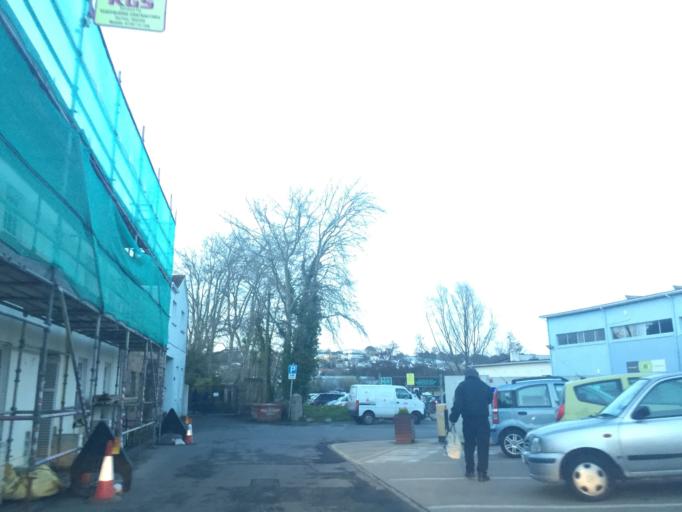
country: JE
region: St Helier
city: Saint Helier
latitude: 49.1974
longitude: -2.1595
